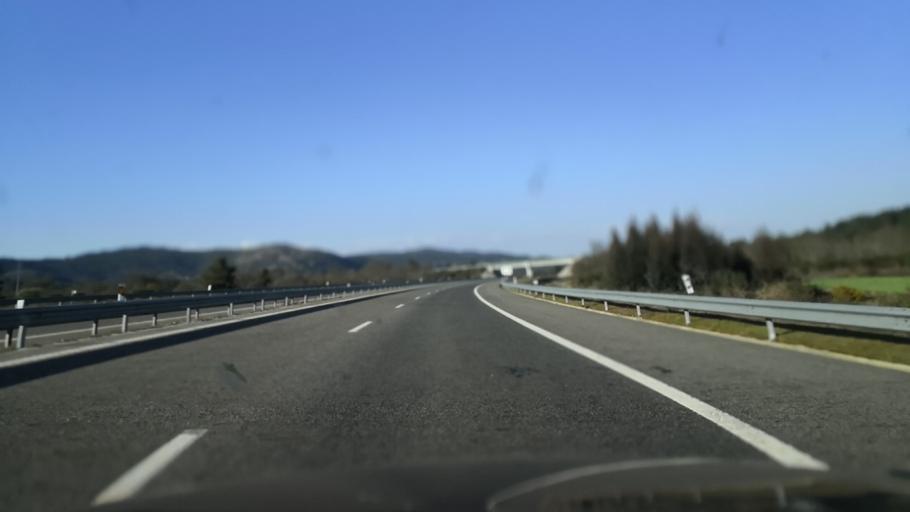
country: PT
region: Vila Real
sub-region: Chaves
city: Chaves
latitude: 41.7465
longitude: -7.5229
